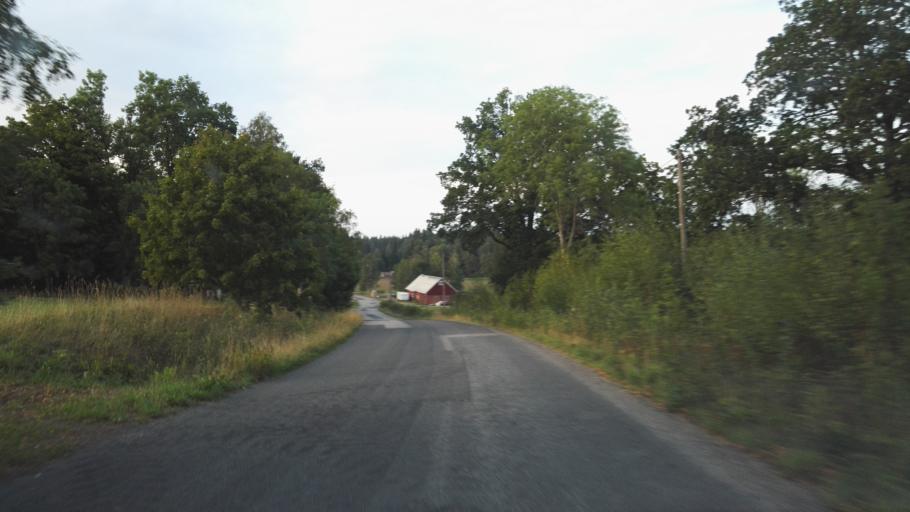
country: SE
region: Joenkoeping
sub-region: Vetlanda Kommun
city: Landsbro
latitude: 57.2591
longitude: 14.8327
